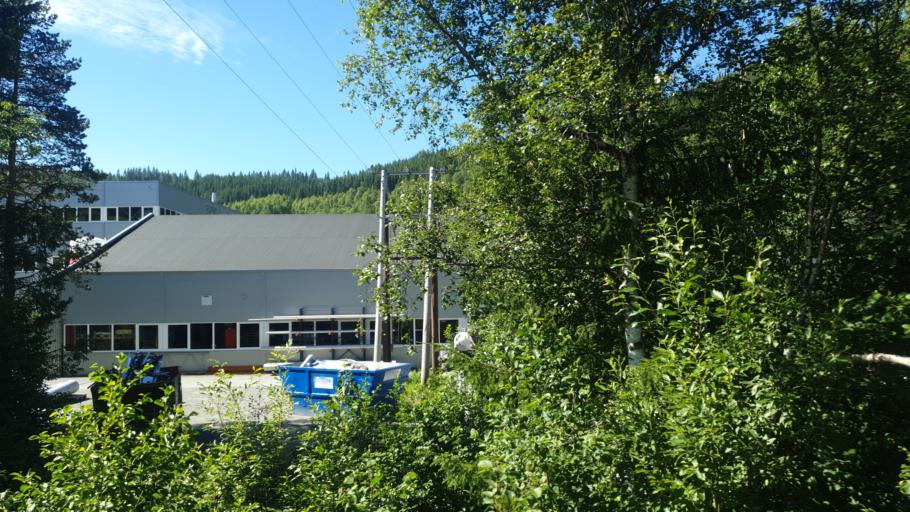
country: NO
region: Sor-Trondelag
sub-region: Meldal
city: Meldal
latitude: 63.1411
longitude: 9.7117
